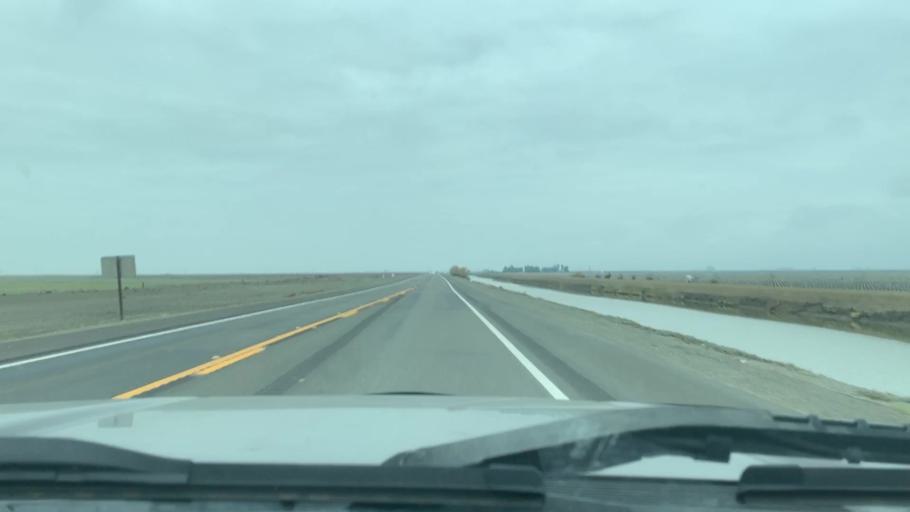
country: US
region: California
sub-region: Kings County
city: Stratford
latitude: 36.1256
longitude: -119.8899
